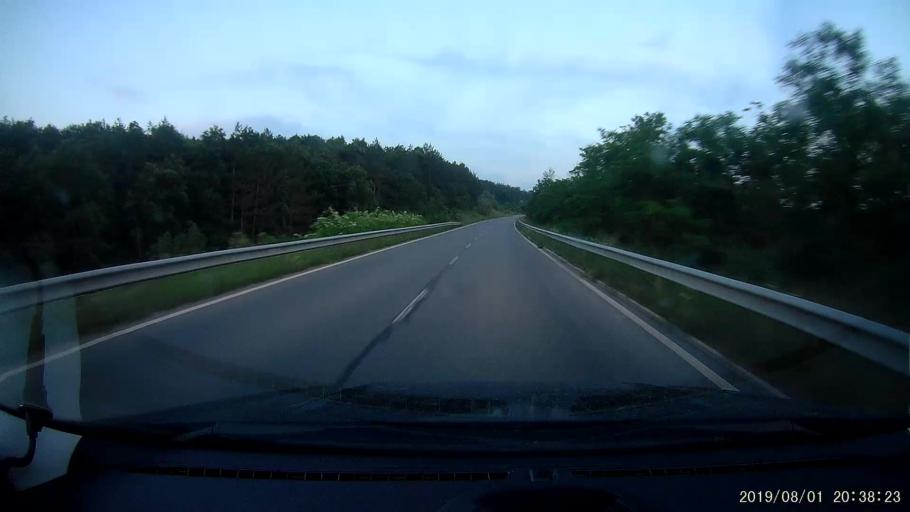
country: BG
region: Yambol
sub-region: Obshtina Elkhovo
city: Elkhovo
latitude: 42.0275
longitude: 26.6010
